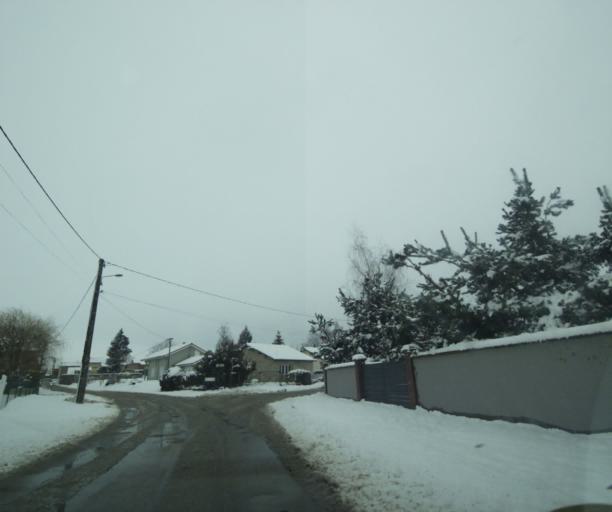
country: FR
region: Champagne-Ardenne
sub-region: Departement de la Haute-Marne
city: Montier-en-Der
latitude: 48.5064
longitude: 4.7869
